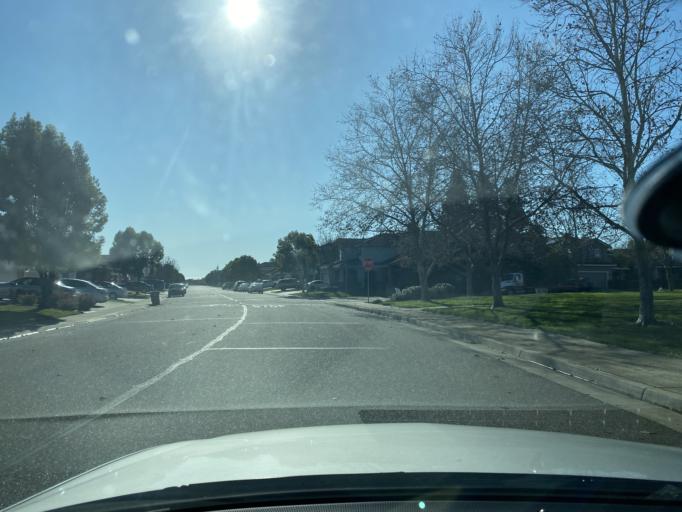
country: US
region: California
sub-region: Sacramento County
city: Laguna
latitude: 38.4366
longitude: -121.3927
